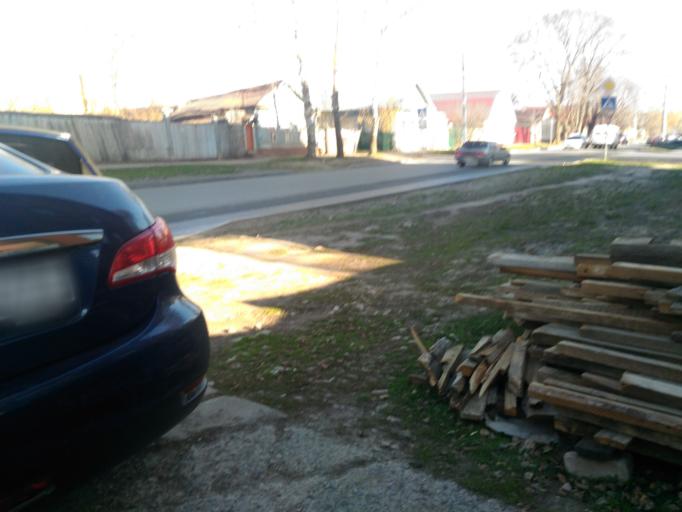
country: RU
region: Ulyanovsk
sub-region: Ulyanovskiy Rayon
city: Ulyanovsk
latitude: 54.3346
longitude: 48.3952
